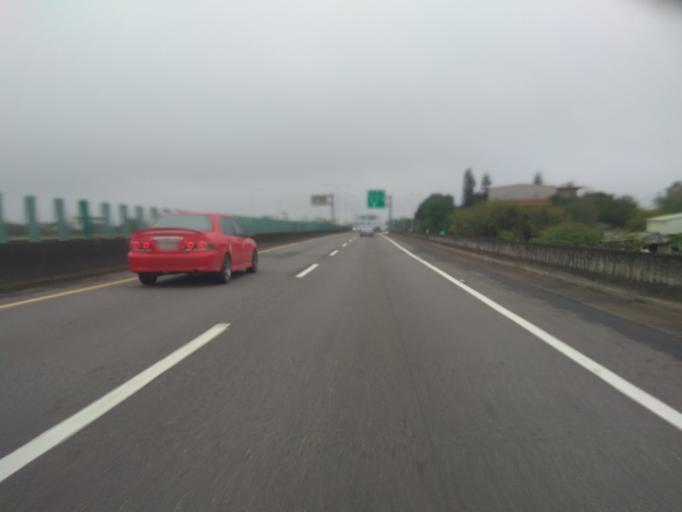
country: TW
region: Taiwan
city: Taoyuan City
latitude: 24.9859
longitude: 121.1261
